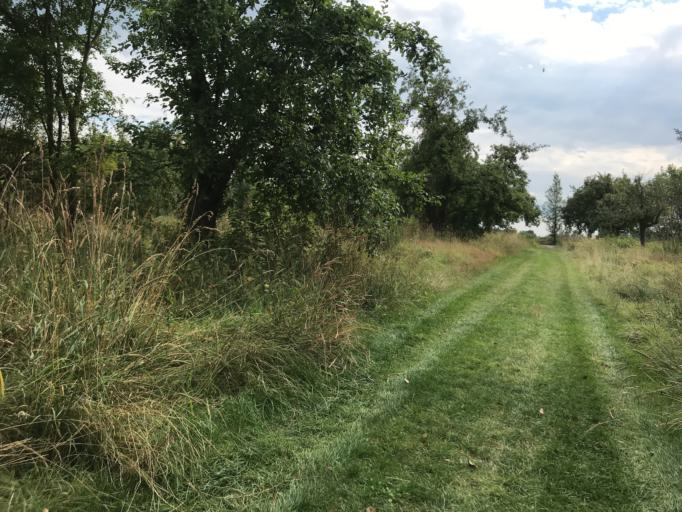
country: CZ
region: Jihocesky
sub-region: Okres Jindrichuv Hradec
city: Lomnice nad Luznici
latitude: 49.0867
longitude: 14.7121
